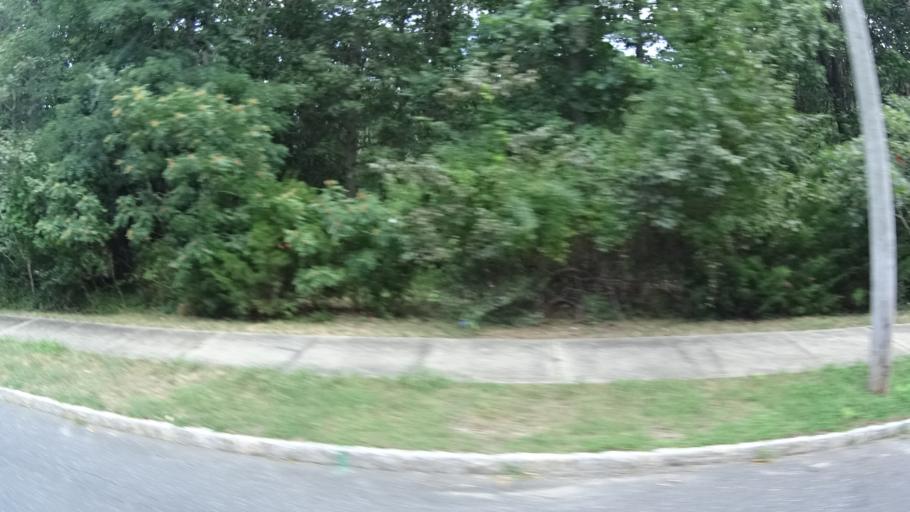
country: US
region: New Jersey
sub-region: Monmouth County
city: Brielle
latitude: 40.1192
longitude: -74.0863
